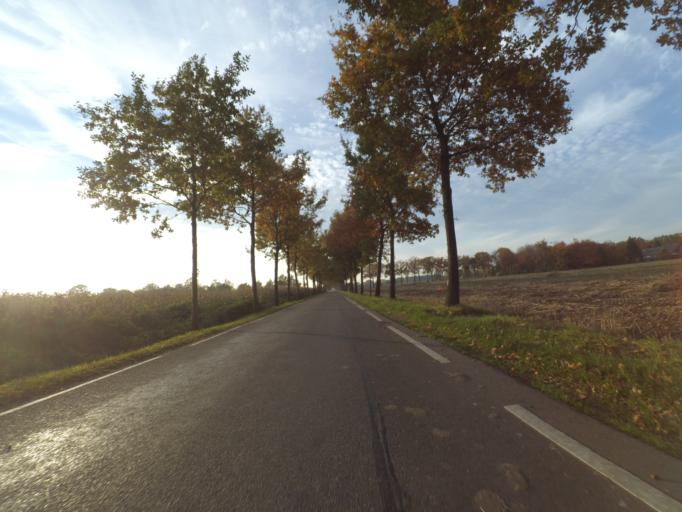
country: NL
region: Utrecht
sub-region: Gemeente Leusden
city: Leusden
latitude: 52.1053
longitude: 5.4578
